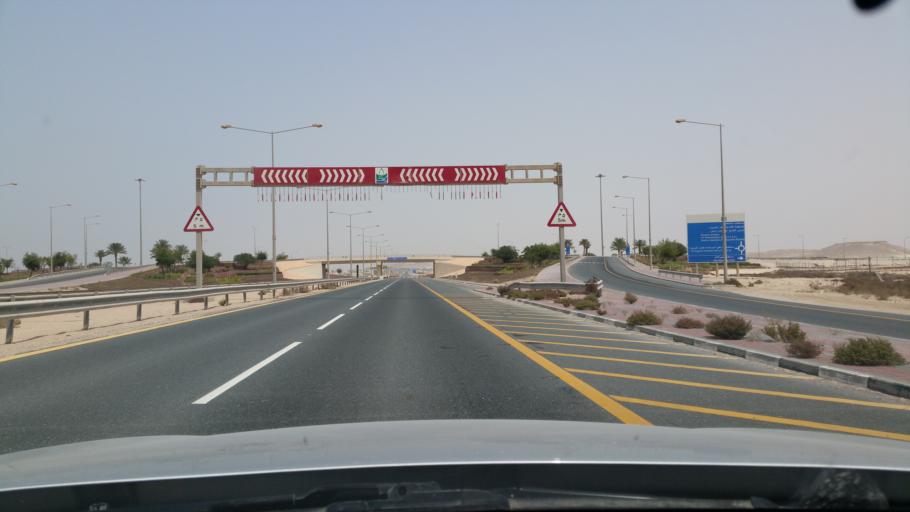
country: QA
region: Baladiyat ar Rayyan
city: Dukhan
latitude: 25.3855
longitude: 50.7823
